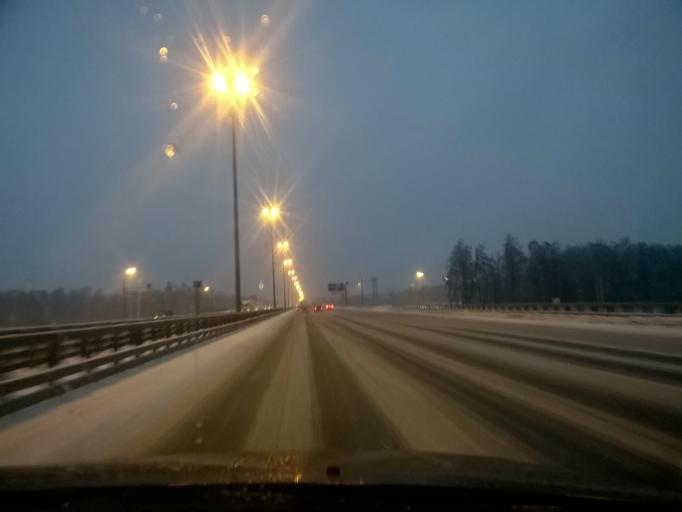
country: RU
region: Moskovskaya
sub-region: Leninskiy Rayon
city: Vnukovo
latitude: 55.5967
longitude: 37.3072
